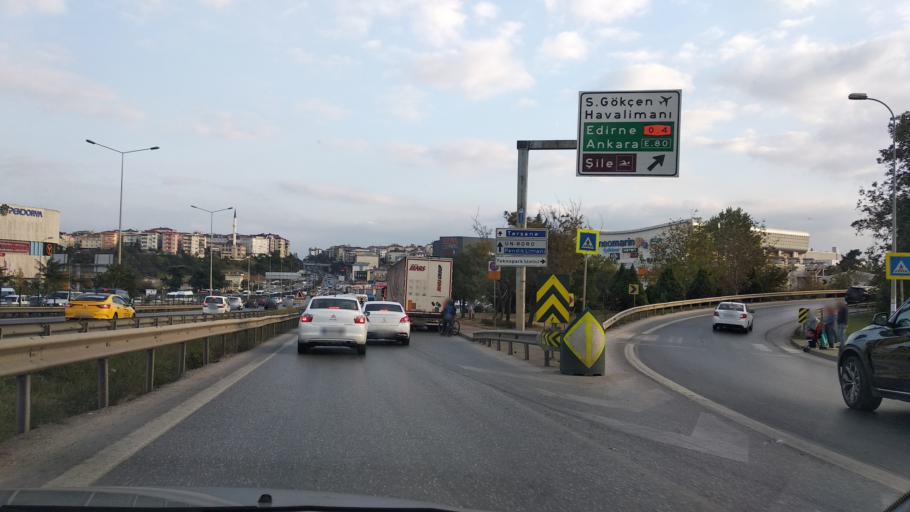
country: TR
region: Istanbul
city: Pendik
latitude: 40.8664
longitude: 29.2726
